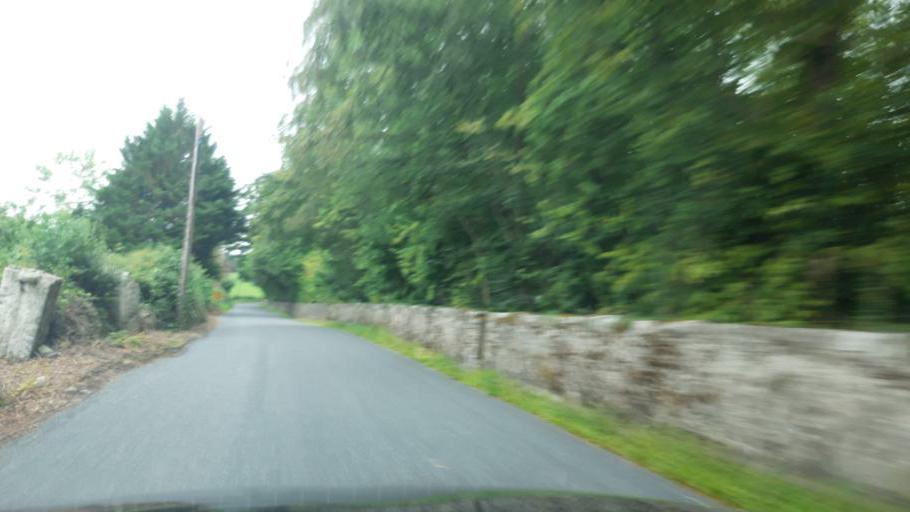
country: IE
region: Leinster
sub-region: Kilkenny
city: Ballyragget
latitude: 52.7264
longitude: -7.3995
